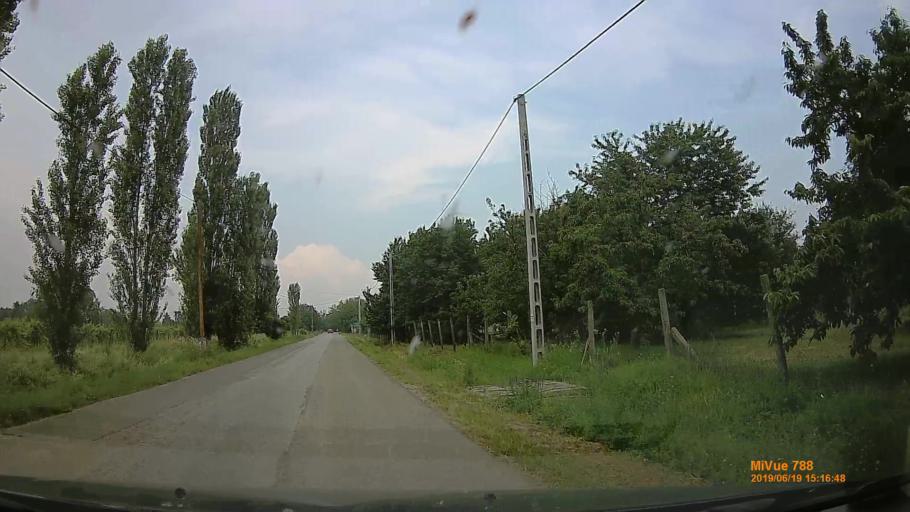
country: HU
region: Baranya
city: Szigetvar
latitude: 46.0792
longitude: 17.8434
